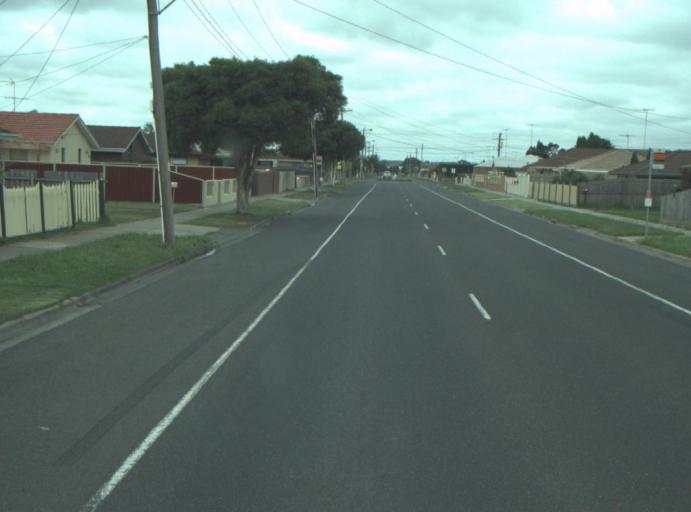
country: AU
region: Victoria
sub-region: Greater Geelong
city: Bell Post Hill
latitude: -38.0712
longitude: 144.3488
